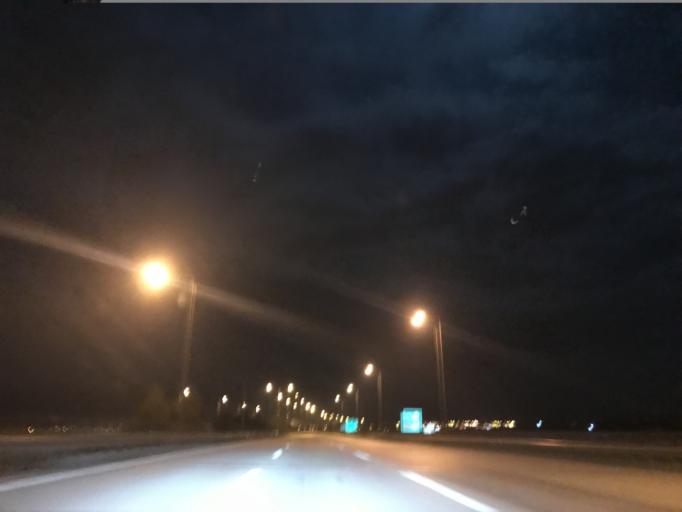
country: TR
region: Hatay
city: Mahmutlar
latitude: 36.9582
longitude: 36.1387
